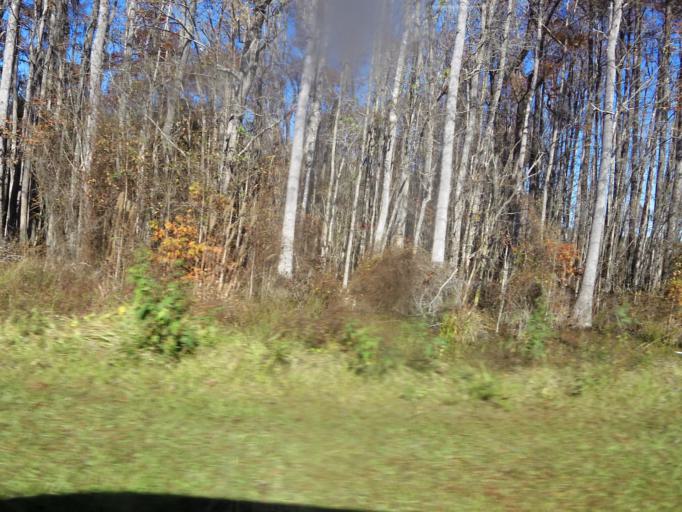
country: US
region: Georgia
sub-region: Liberty County
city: Midway
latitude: 31.7999
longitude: -81.4319
